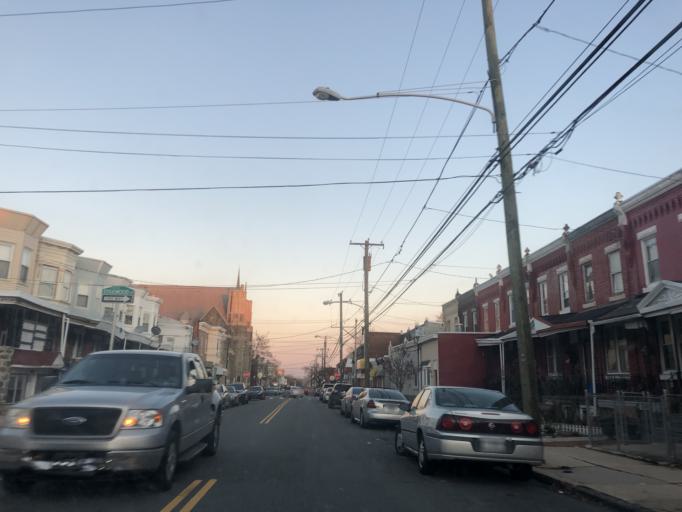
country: US
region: Pennsylvania
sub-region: Delaware County
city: Millbourne
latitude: 39.9727
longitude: -75.2406
